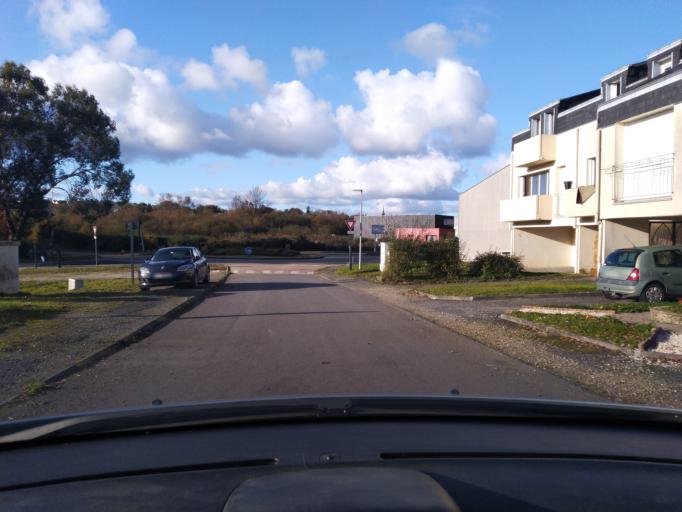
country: FR
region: Brittany
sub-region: Departement du Finistere
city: Guerlesquin
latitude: 48.5120
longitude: -3.5841
